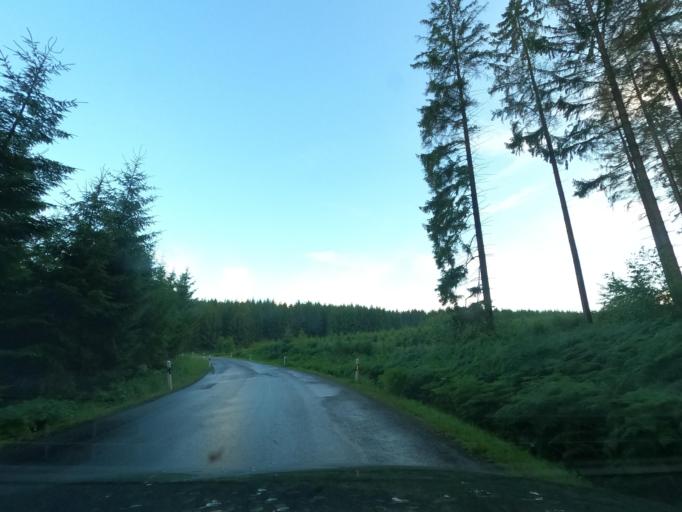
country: DE
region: North Rhine-Westphalia
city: Plettenberg
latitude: 51.2550
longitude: 7.9207
